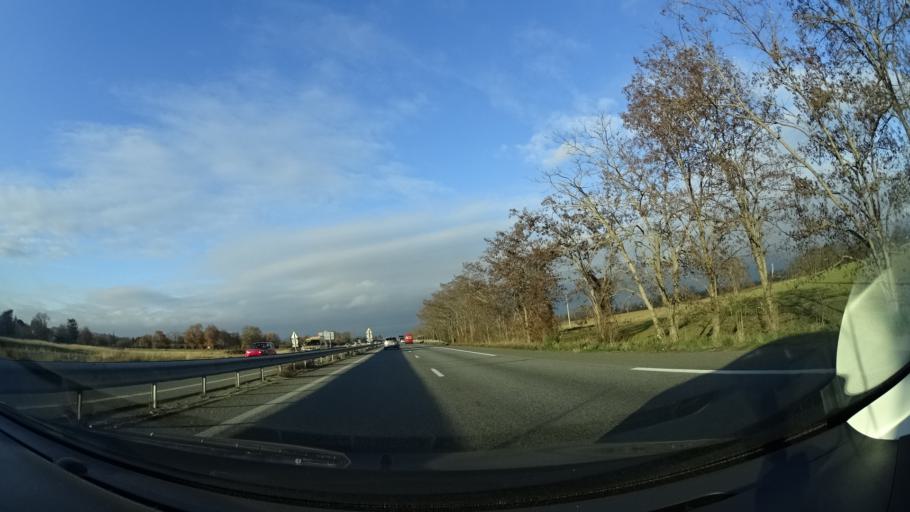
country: FR
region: Midi-Pyrenees
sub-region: Departement de l'Ariege
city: Saint-Jean-du-Falga
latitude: 43.0950
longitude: 1.6335
